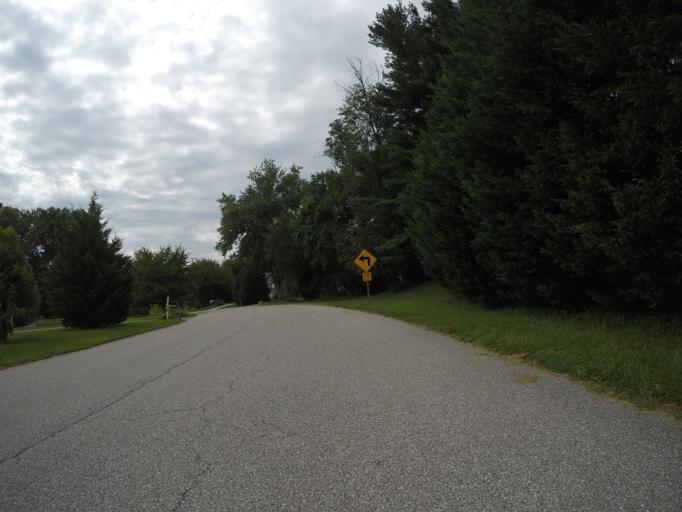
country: US
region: Maryland
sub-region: Howard County
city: Columbia
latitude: 39.2445
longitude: -76.8300
